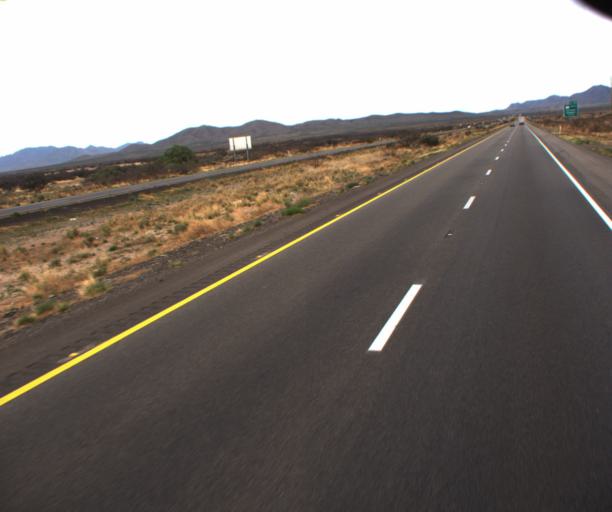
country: US
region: Arizona
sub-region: Cochise County
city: Willcox
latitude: 32.1855
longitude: -109.9346
